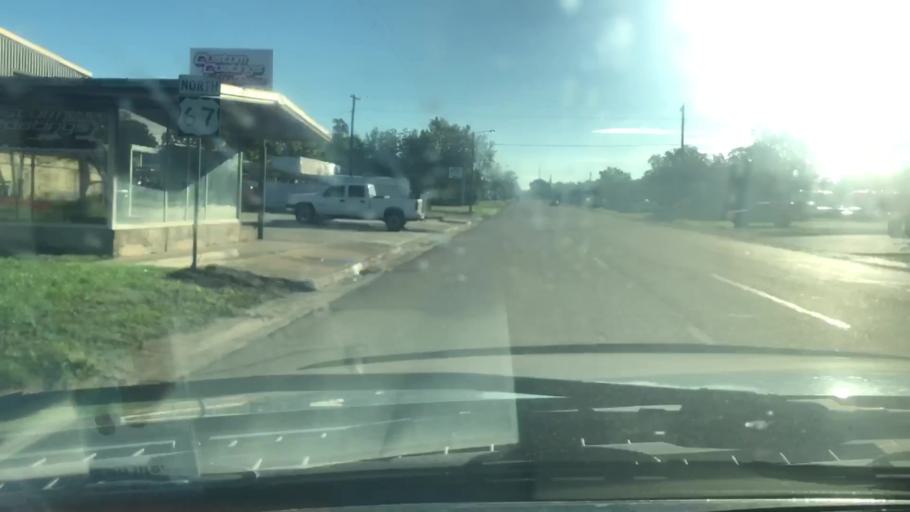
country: US
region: Texas
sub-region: Bowie County
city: Texarkana
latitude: 33.4232
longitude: -94.0669
